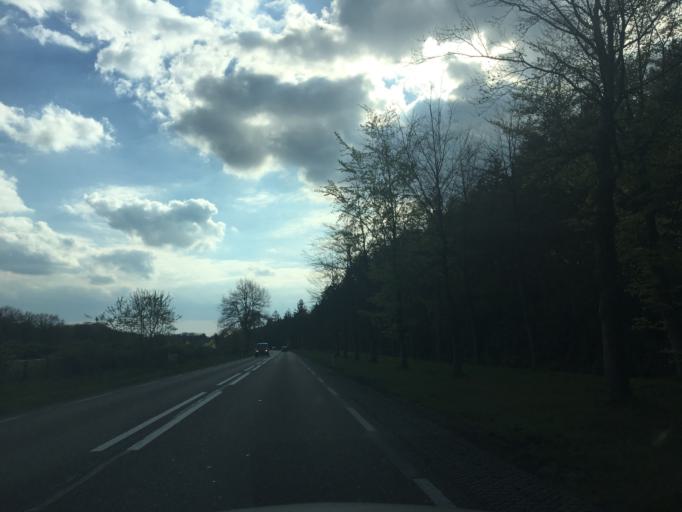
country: NL
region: Utrecht
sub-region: Gemeente Soest
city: Soest
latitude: 52.1894
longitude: 5.2724
